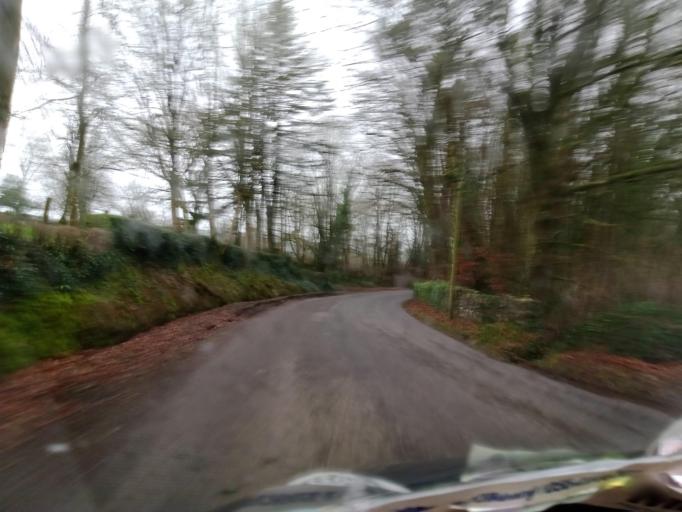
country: IE
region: Munster
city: Fethard
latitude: 52.5542
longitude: -7.7623
